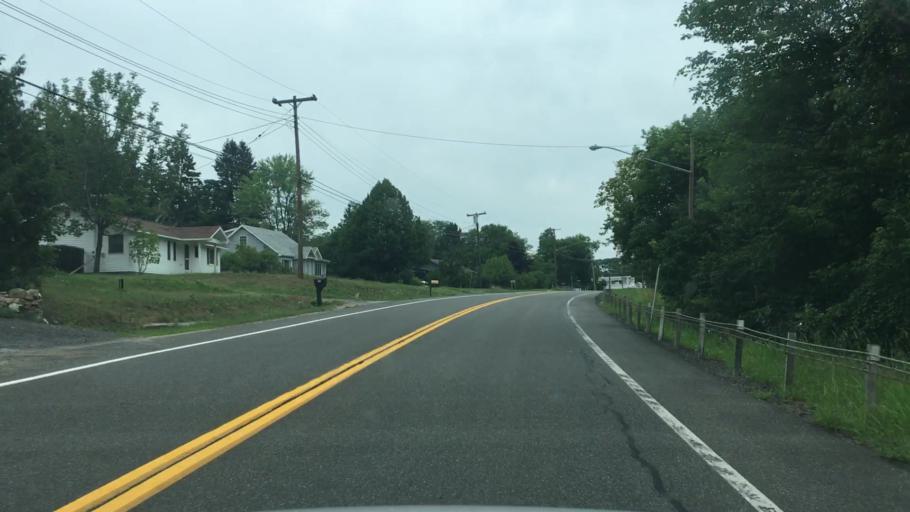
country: US
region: New York
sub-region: Essex County
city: Keeseville
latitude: 44.4991
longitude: -73.4948
